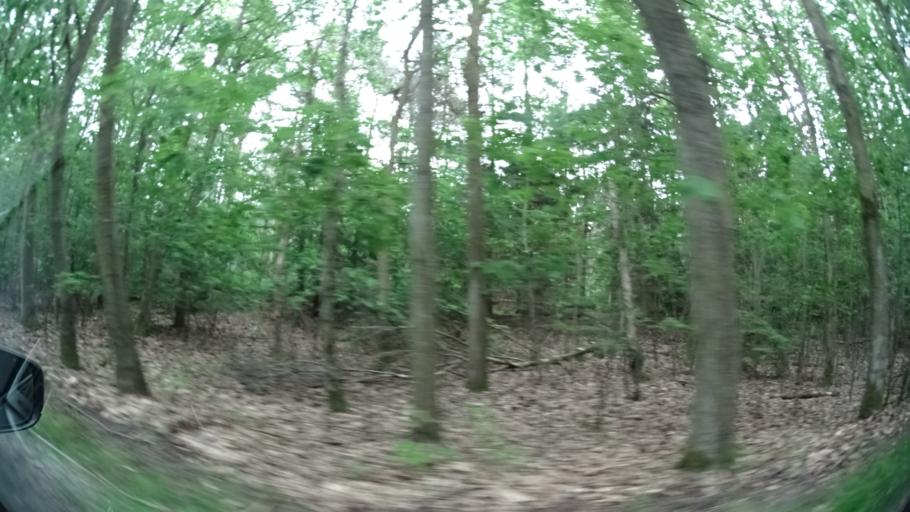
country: DK
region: Central Jutland
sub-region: Norddjurs Kommune
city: Grenaa
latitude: 56.4937
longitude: 10.7388
